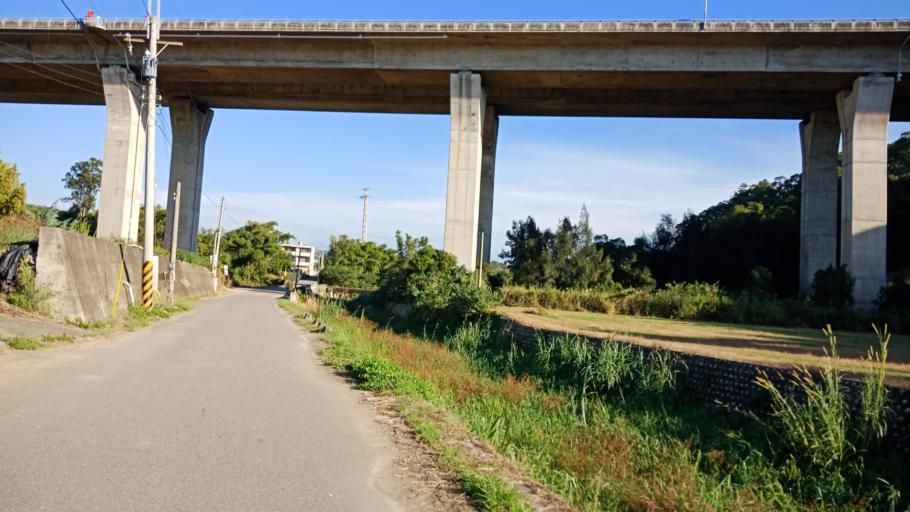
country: TW
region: Taiwan
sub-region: Miaoli
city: Miaoli
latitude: 24.4850
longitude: 120.7000
